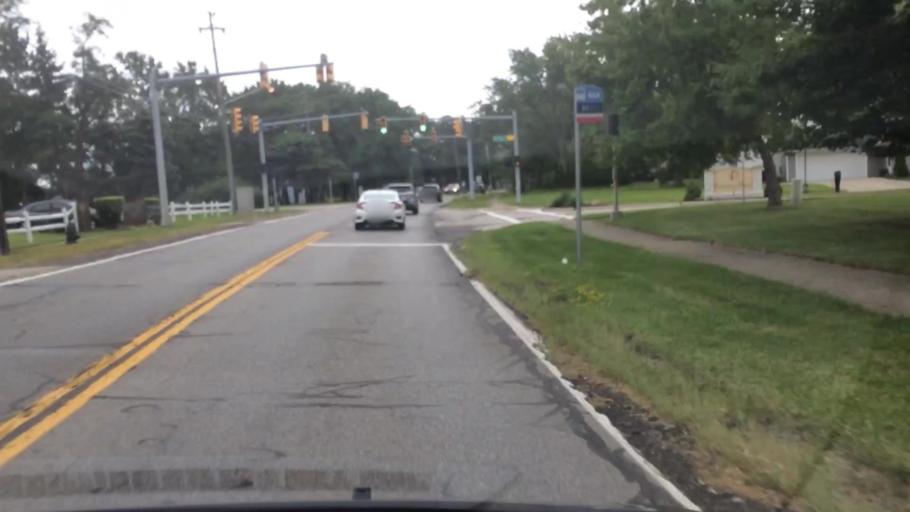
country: US
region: Ohio
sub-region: Cuyahoga County
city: Strongsville
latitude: 41.3054
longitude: -81.8114
